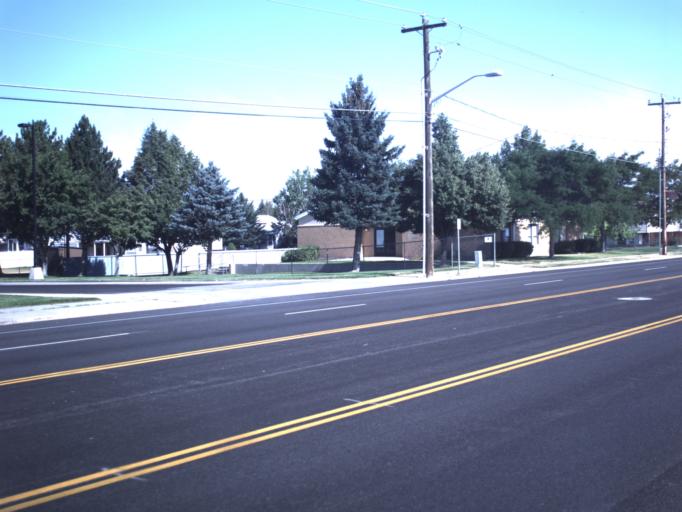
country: US
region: Utah
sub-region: Salt Lake County
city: Oquirrh
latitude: 40.6456
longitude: -112.0245
